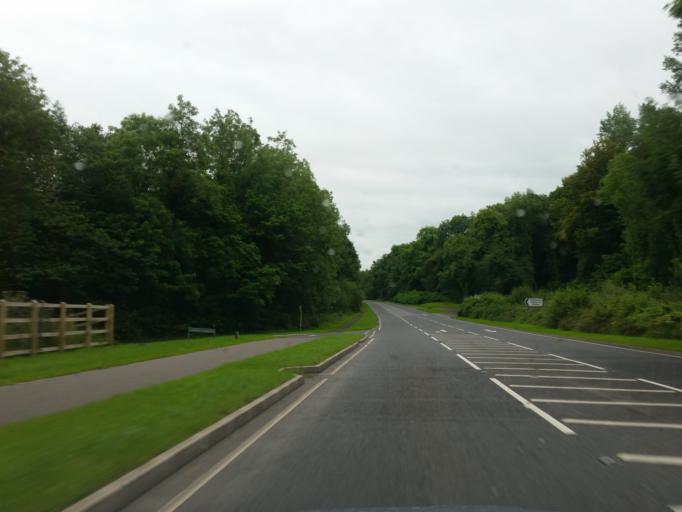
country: GB
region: Northern Ireland
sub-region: Fermanagh District
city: Enniskillen
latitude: 54.3276
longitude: -7.6156
